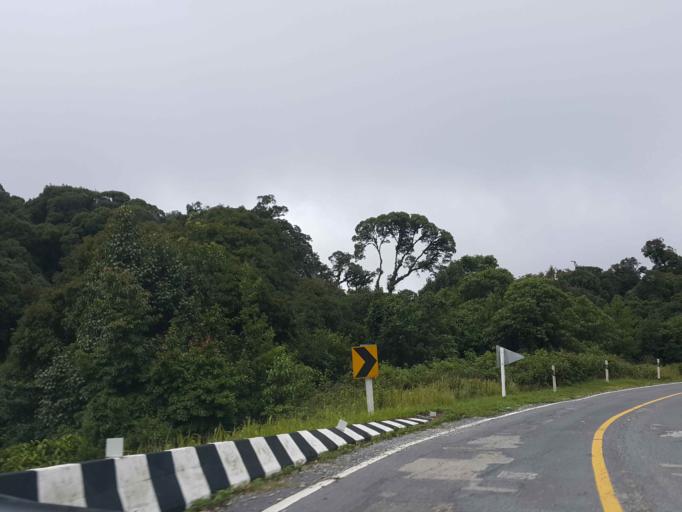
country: TH
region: Chiang Mai
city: Mae Chaem
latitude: 18.5697
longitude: 98.4849
